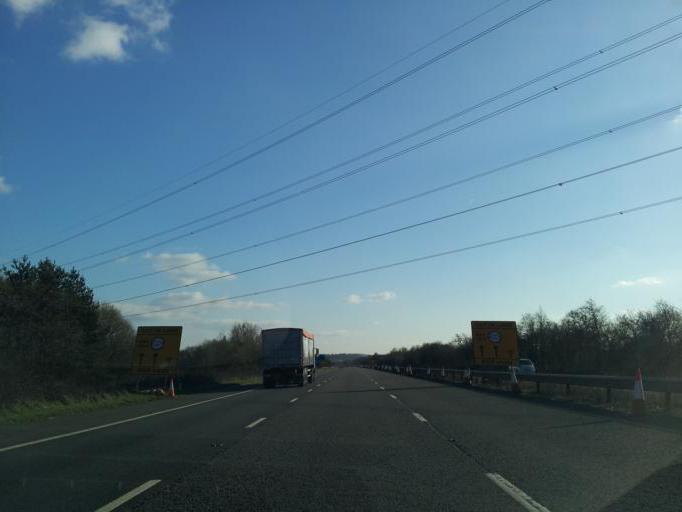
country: GB
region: England
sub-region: Devon
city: Cullompton
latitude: 50.8746
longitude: -3.3816
